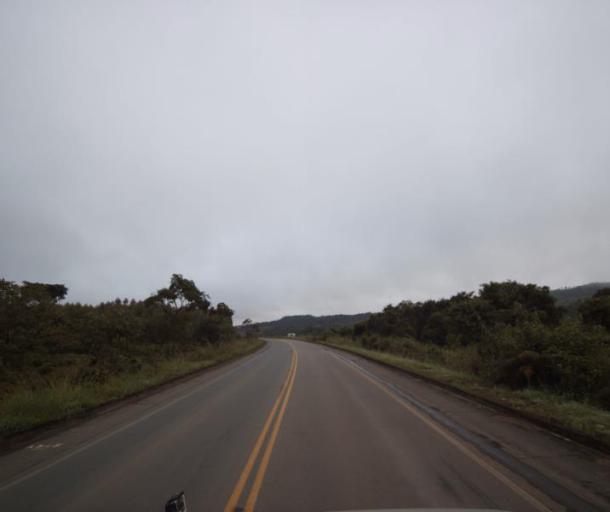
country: BR
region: Goias
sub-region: Pirenopolis
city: Pirenopolis
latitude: -15.8219
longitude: -48.7785
